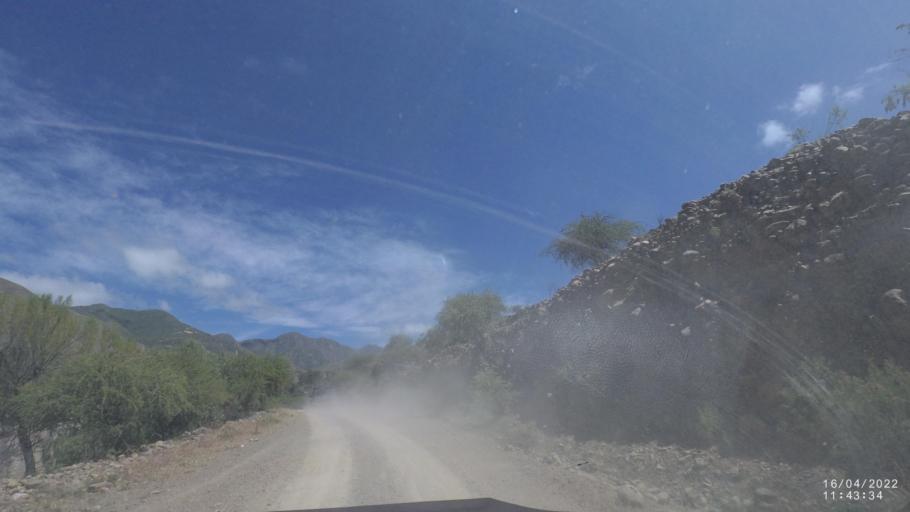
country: BO
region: Cochabamba
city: Mizque
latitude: -17.9818
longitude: -65.6292
